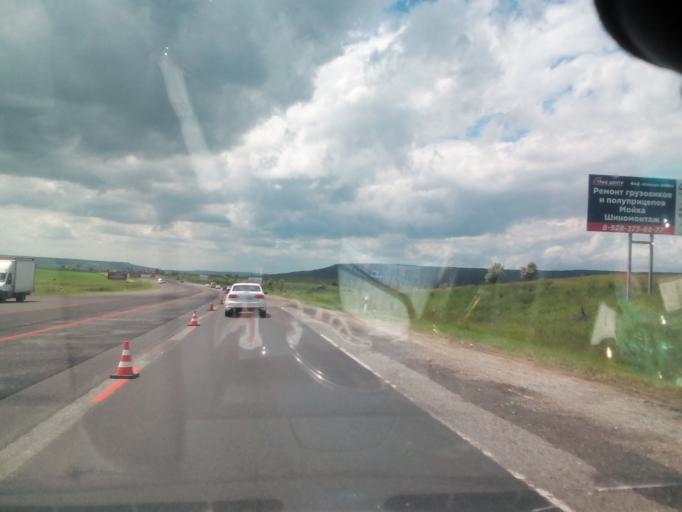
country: RU
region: Stavropol'skiy
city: Tatarka
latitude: 44.9511
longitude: 41.9392
